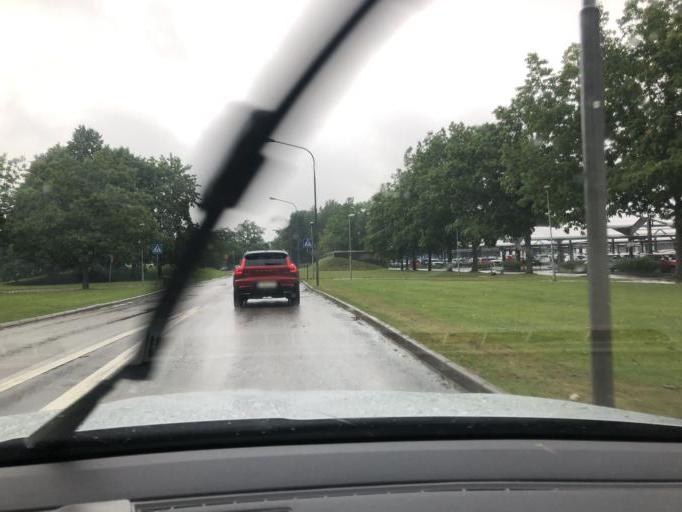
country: SE
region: Vaestra Goetaland
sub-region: Skovde Kommun
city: Skoevde
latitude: 58.4260
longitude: 13.8545
